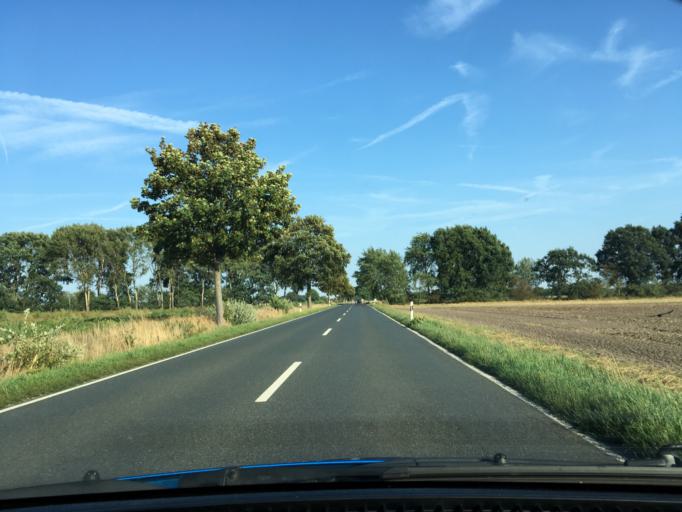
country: DE
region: Lower Saxony
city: Isernhagen Farster Bauerschaft
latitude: 52.4829
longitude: 9.8861
